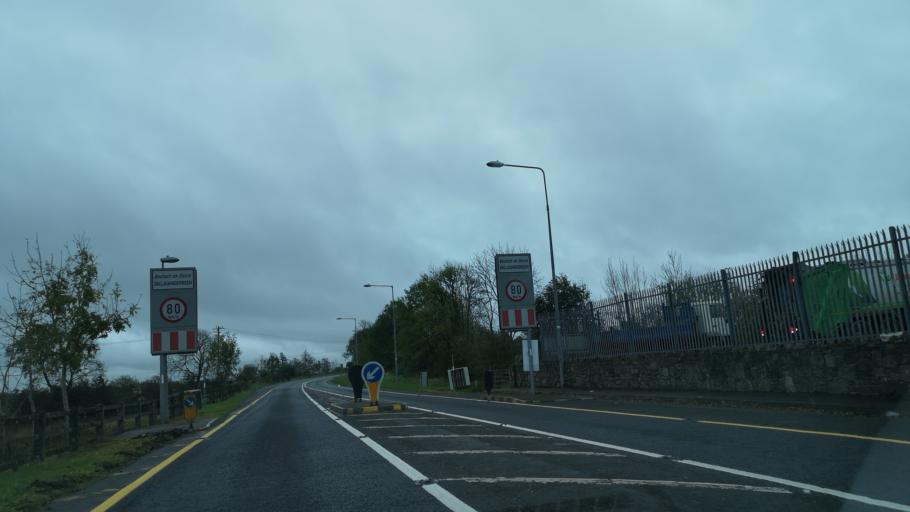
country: IE
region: Connaught
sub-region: Roscommon
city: Ballaghaderreen
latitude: 53.8968
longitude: -8.5661
